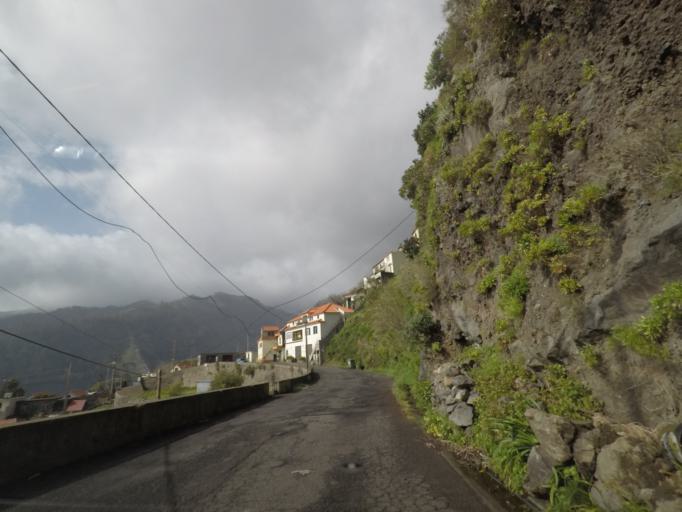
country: PT
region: Madeira
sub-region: Ribeira Brava
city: Campanario
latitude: 32.7052
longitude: -17.0287
